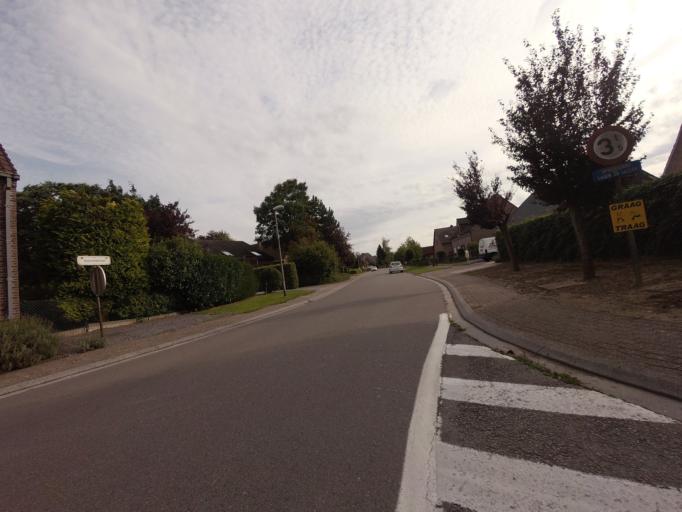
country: BE
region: Flanders
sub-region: Provincie Vlaams-Brabant
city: Meise
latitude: 50.9589
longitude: 4.3349
